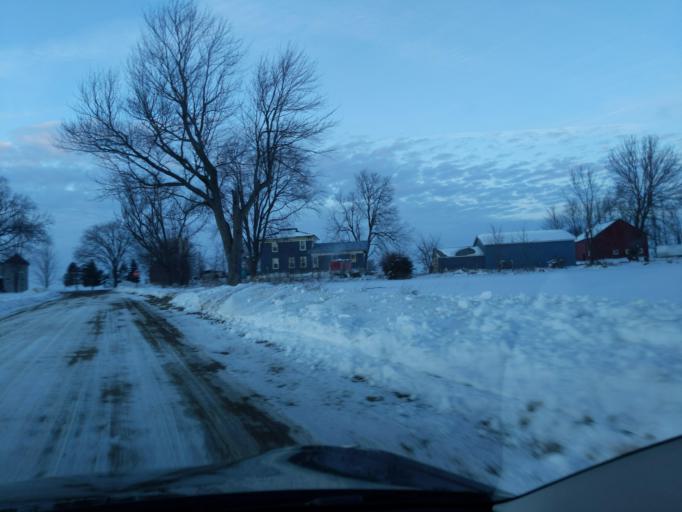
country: US
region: Michigan
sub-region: Ingham County
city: Williamston
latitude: 42.5751
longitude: -84.3175
